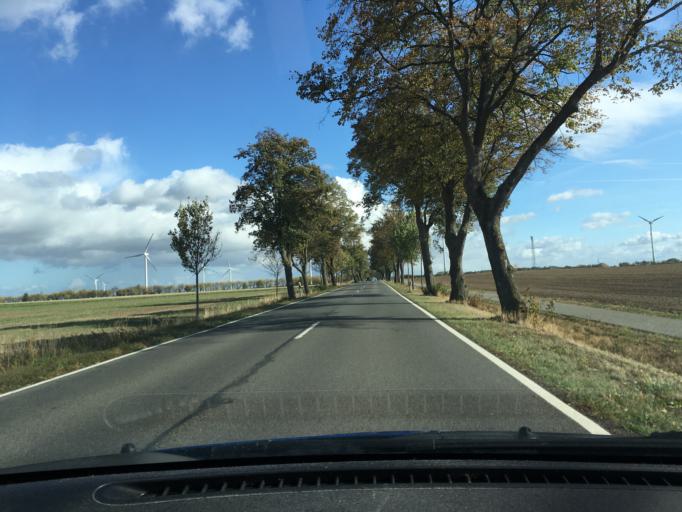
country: DE
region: Saxony-Anhalt
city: Pretzier
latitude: 52.8403
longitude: 11.2130
